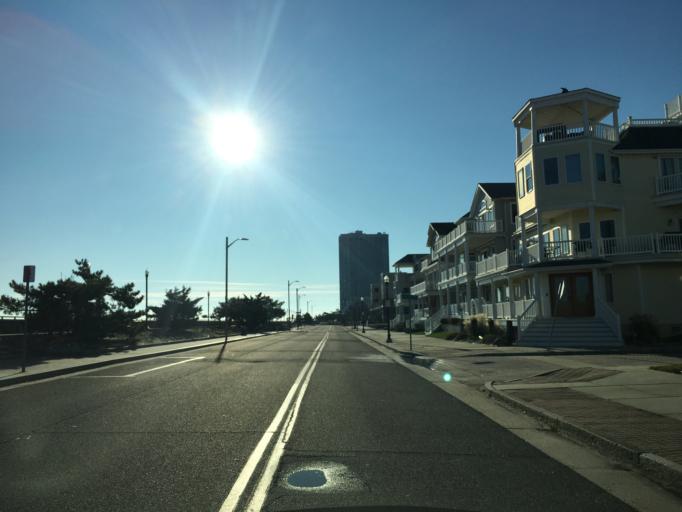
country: US
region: New Jersey
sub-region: Atlantic County
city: Atlantic City
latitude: 39.3751
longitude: -74.4158
